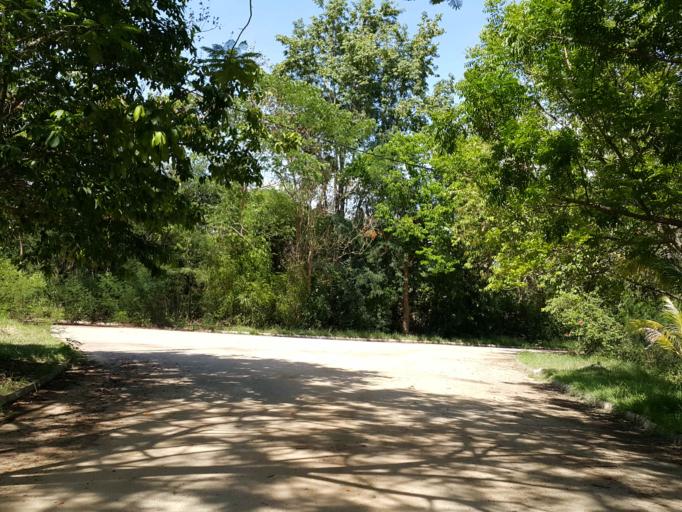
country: TH
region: Chiang Mai
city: San Kamphaeng
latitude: 18.7602
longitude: 99.1121
